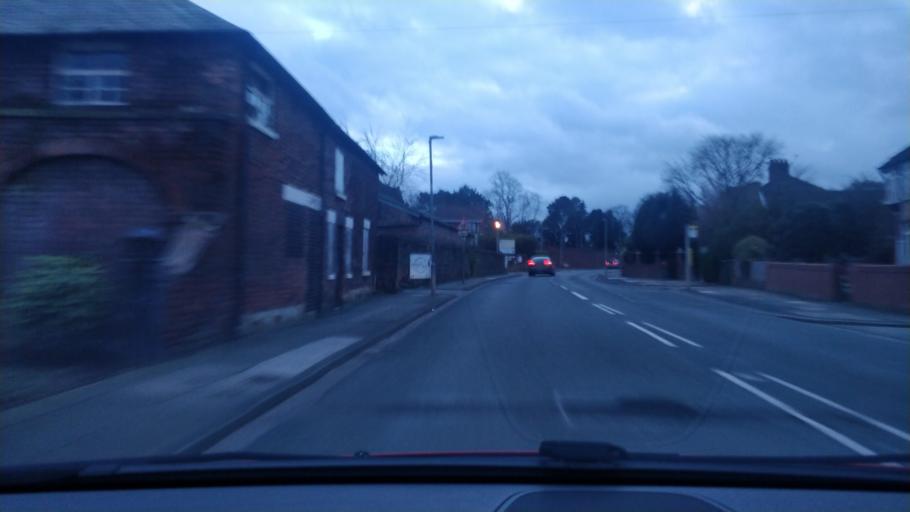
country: GB
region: England
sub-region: Knowsley
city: Knowsley
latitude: 53.4271
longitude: -2.8862
